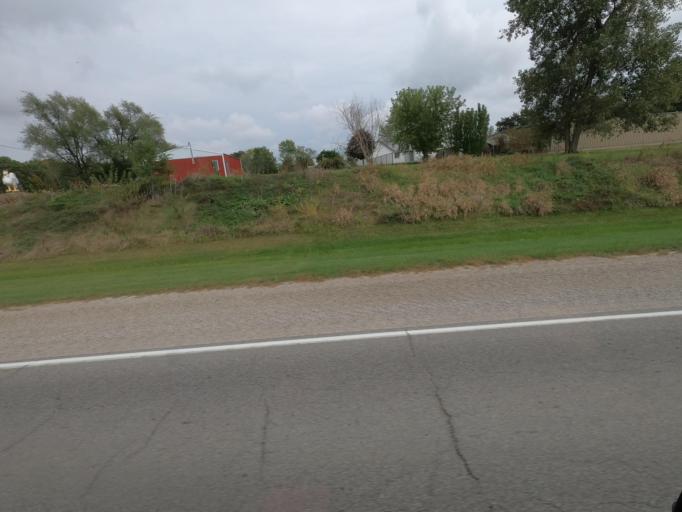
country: US
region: Iowa
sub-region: Wapello County
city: Ottumwa
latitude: 40.9350
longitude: -92.2275
